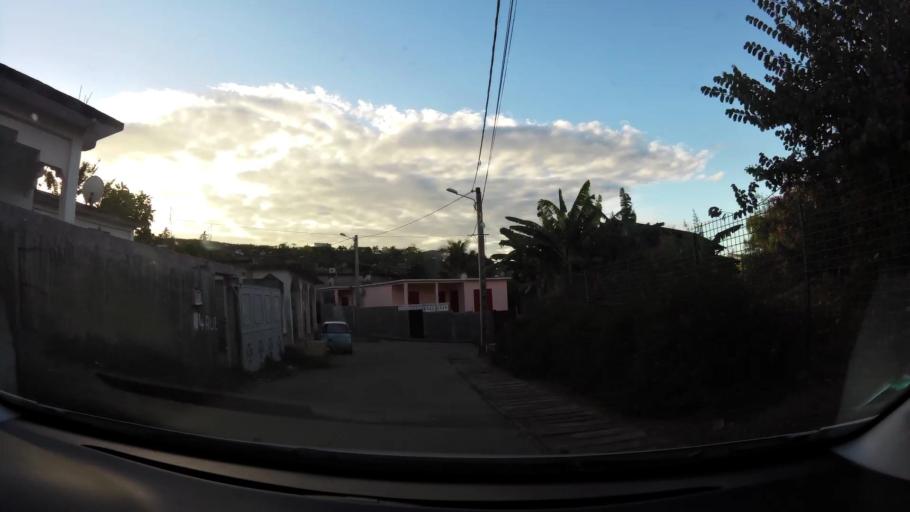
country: YT
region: Koungou
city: Koungou
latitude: -12.7359
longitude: 45.1982
